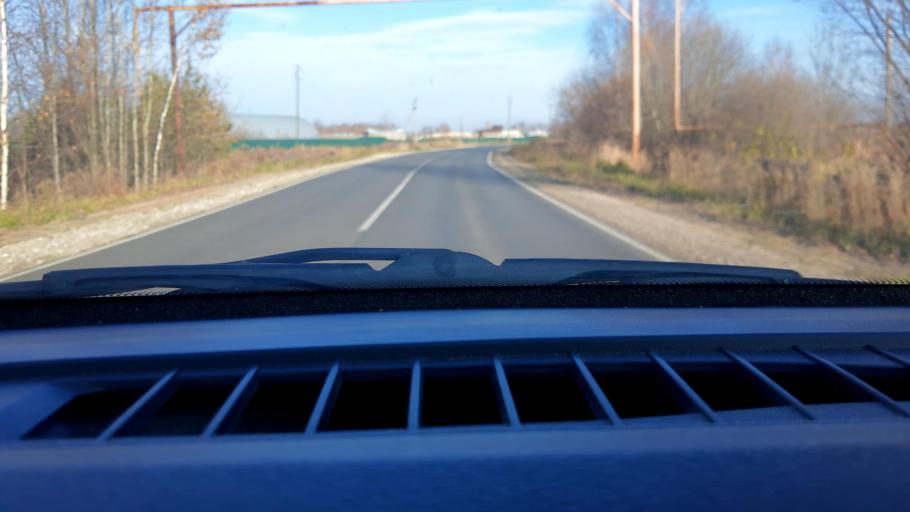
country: RU
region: Nizjnij Novgorod
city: Neklyudovo
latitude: 56.4491
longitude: 43.9001
